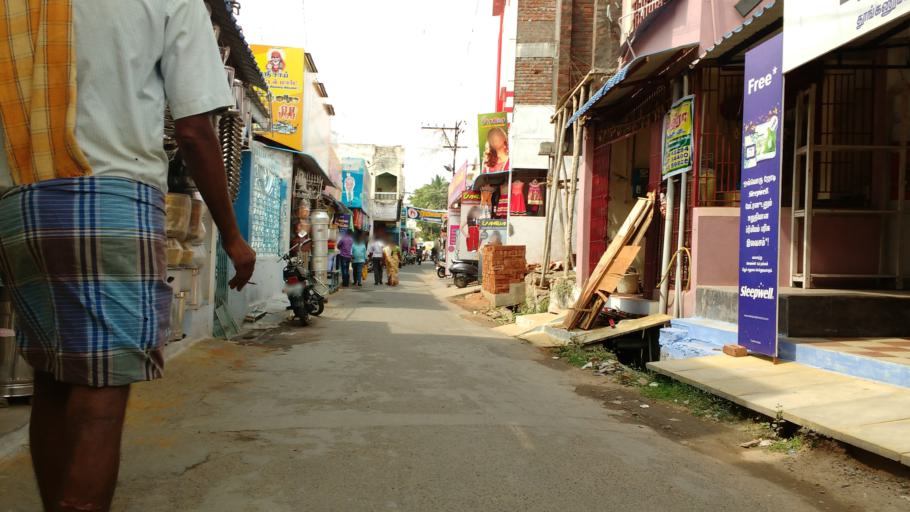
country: IN
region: Tamil Nadu
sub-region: Erode
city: Gobichettipalayam
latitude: 11.4558
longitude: 77.4357
